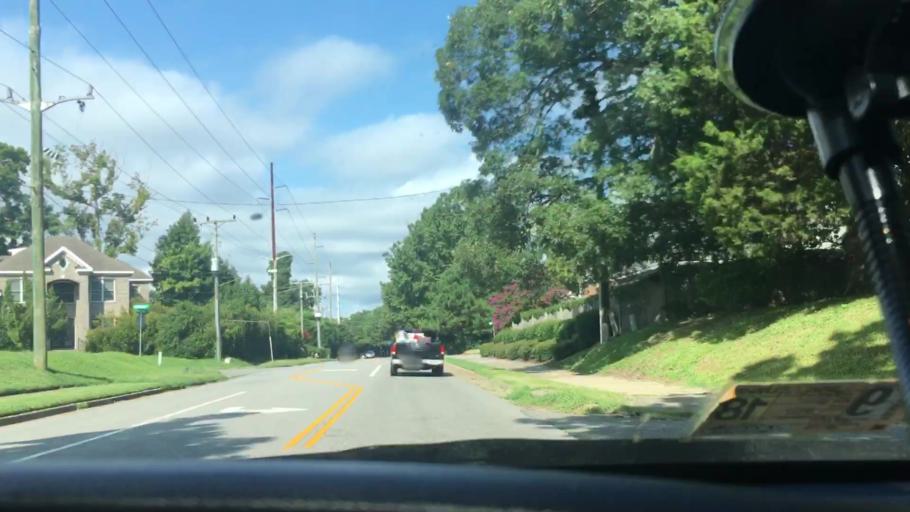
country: US
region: Virginia
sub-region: City of Virginia Beach
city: Virginia Beach
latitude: 36.8798
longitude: -76.0364
